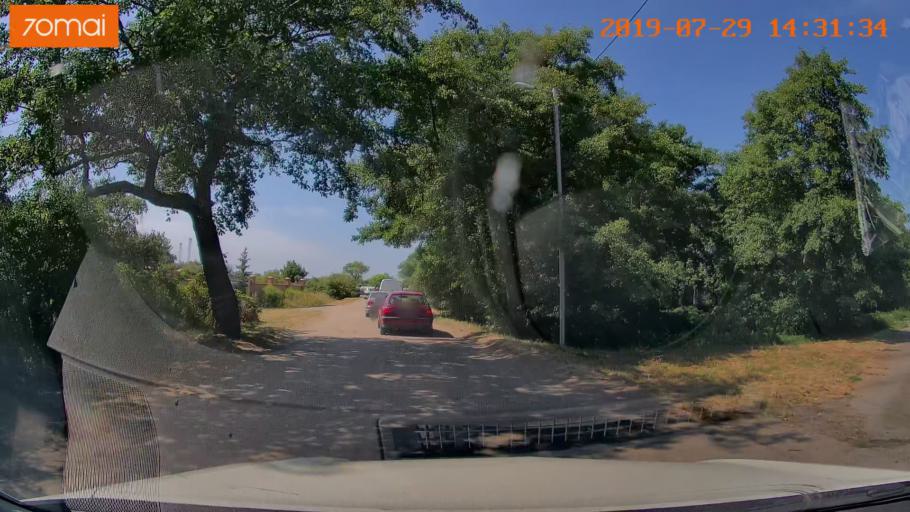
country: RU
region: Kaliningrad
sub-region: Gorod Kaliningrad
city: Baltiysk
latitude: 54.6458
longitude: 19.8813
